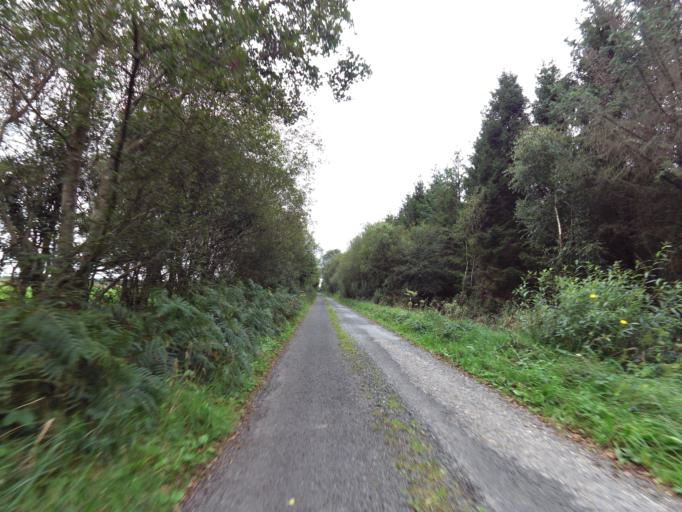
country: IE
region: Leinster
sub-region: Uibh Fhaili
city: Ferbane
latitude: 53.2474
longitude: -7.7389
